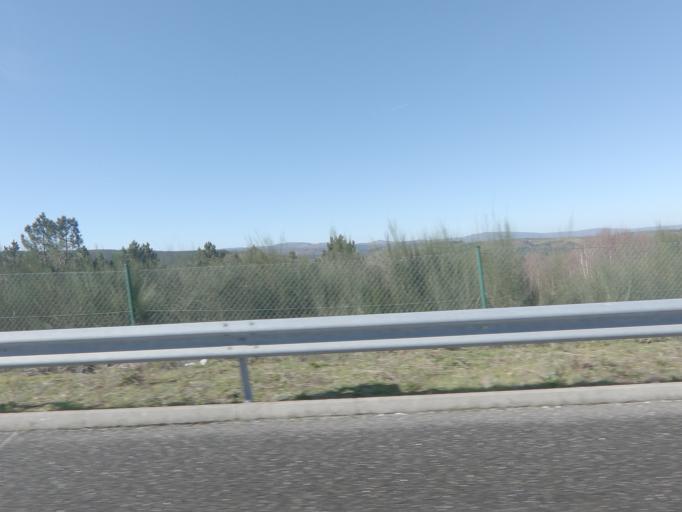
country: ES
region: Galicia
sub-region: Provincia de Pontevedra
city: Dozon
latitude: 42.5753
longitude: -8.0617
